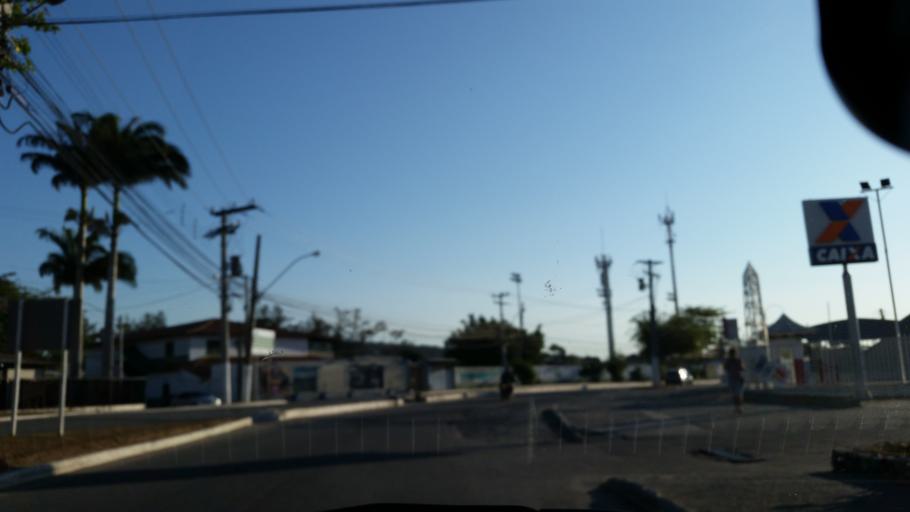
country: BR
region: Rio de Janeiro
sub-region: Armacao De Buzios
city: Armacao de Buzios
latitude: -22.7740
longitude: -41.9143
